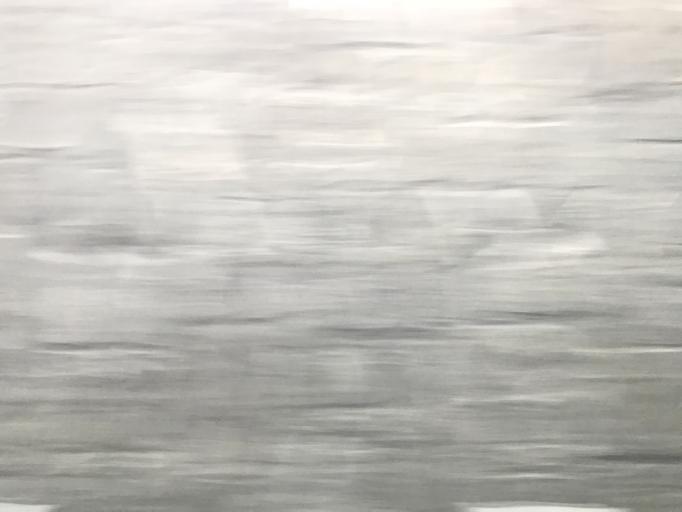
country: ES
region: Basque Country
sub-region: Provincia de Guipuzcoa
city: Villafranca de Ordizia
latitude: 43.0540
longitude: -2.1726
